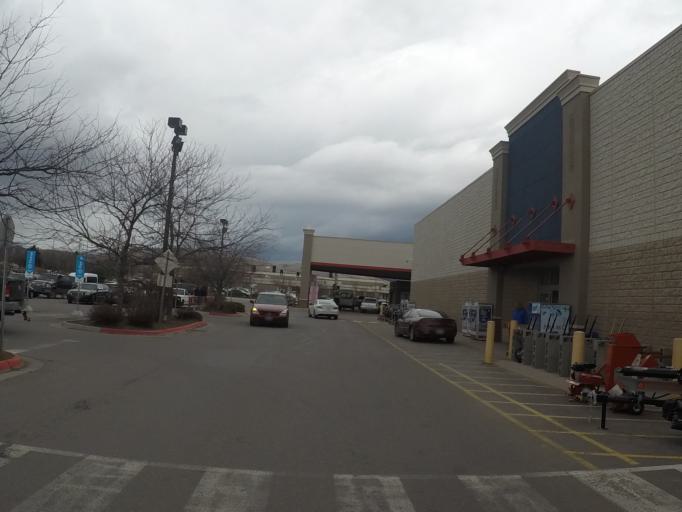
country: US
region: Montana
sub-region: Missoula County
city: Orchard Homes
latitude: 46.8929
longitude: -114.0374
